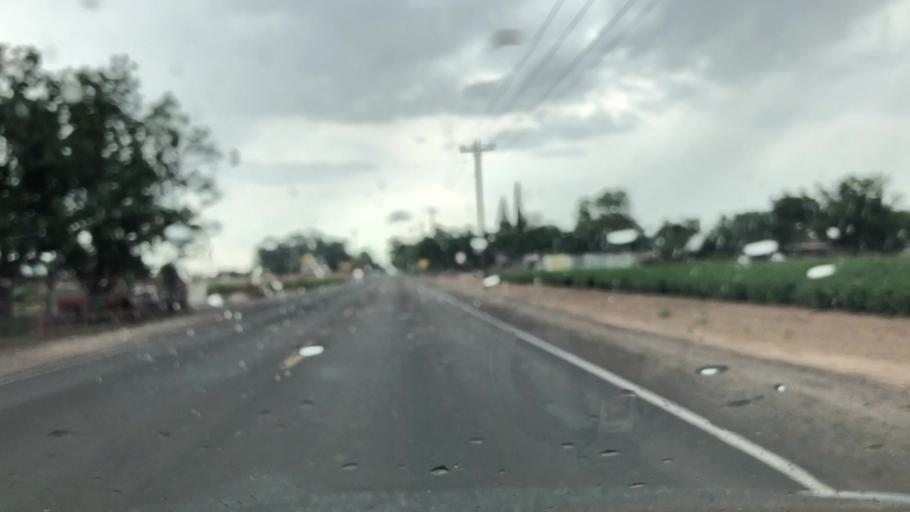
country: US
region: New Mexico
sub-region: Dona Ana County
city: Vado
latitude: 32.1091
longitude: -106.6835
